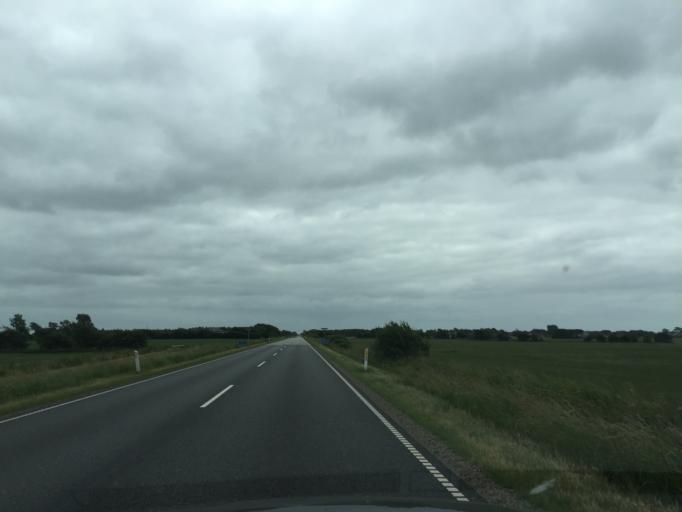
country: DK
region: South Denmark
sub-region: Esbjerg Kommune
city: Ribe
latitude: 55.2454
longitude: 8.7234
